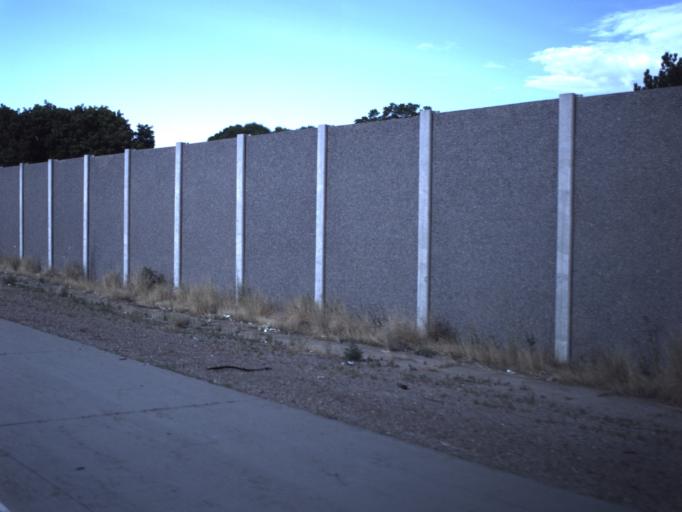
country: US
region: Utah
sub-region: Salt Lake County
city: Taylorsville
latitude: 40.6596
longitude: -111.9524
